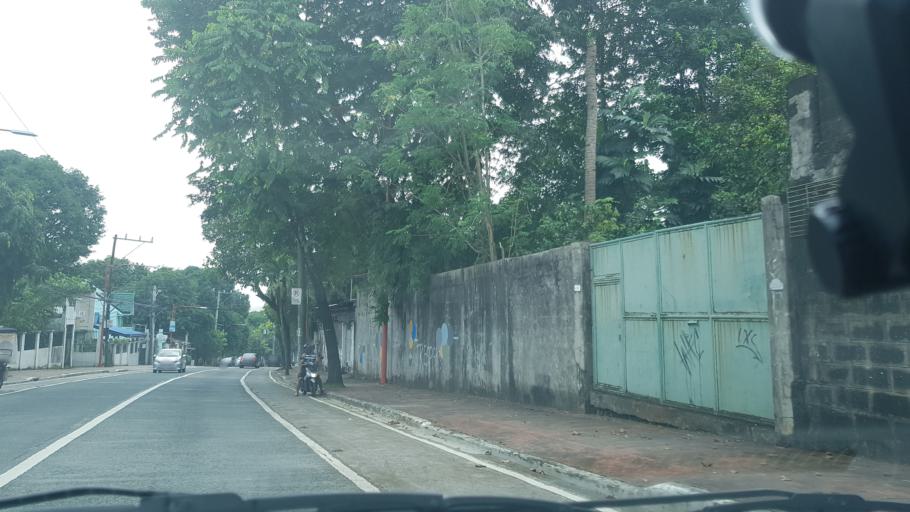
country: PH
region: Calabarzon
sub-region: Province of Rizal
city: Antipolo
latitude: 14.6535
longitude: 121.1230
